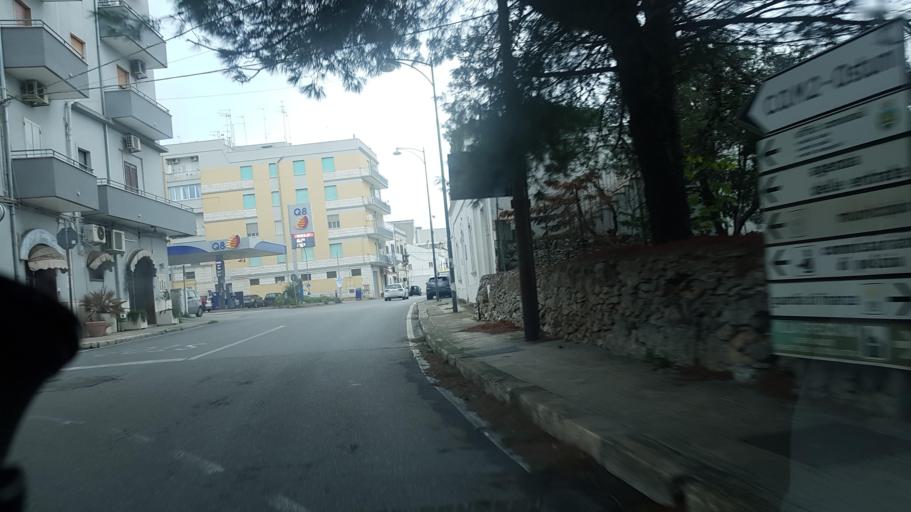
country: IT
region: Apulia
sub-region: Provincia di Brindisi
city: Ostuni
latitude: 40.7260
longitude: 17.5851
